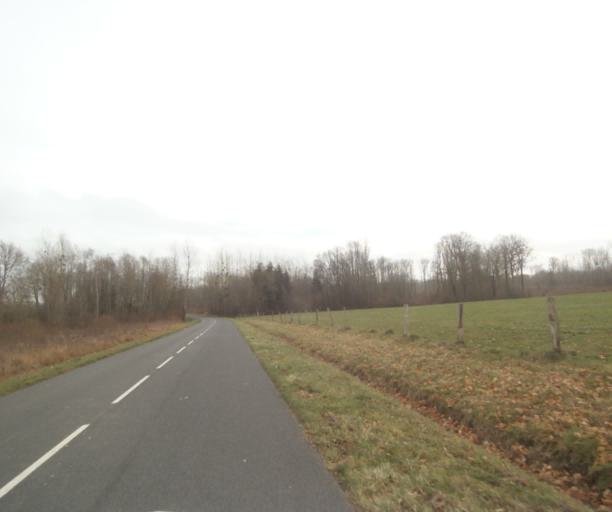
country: FR
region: Champagne-Ardenne
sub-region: Departement de la Marne
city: Pargny-sur-Saulx
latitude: 48.7414
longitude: 4.8629
